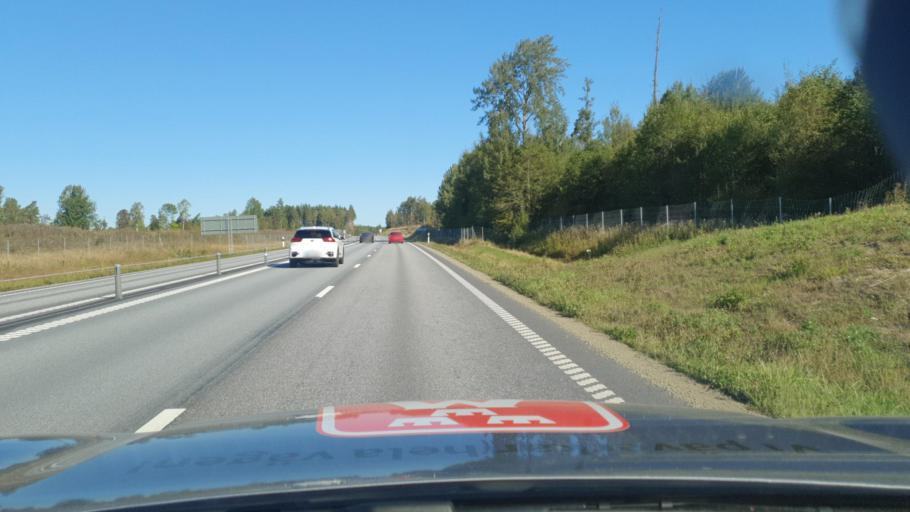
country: SE
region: OErebro
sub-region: Hallsbergs Kommun
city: Palsboda
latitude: 59.0827
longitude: 15.3093
